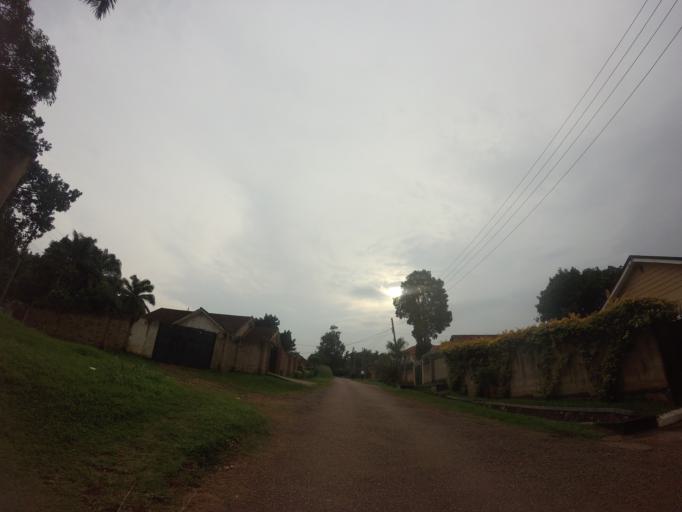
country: UG
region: Central Region
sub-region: Wakiso District
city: Kireka
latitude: 0.3479
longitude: 32.6211
